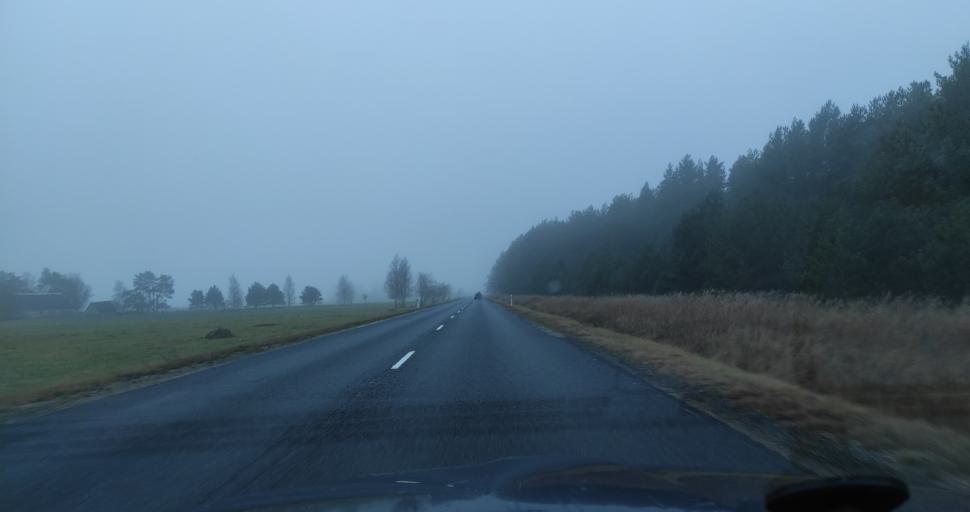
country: LV
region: Alsunga
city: Alsunga
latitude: 57.1076
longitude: 21.4228
